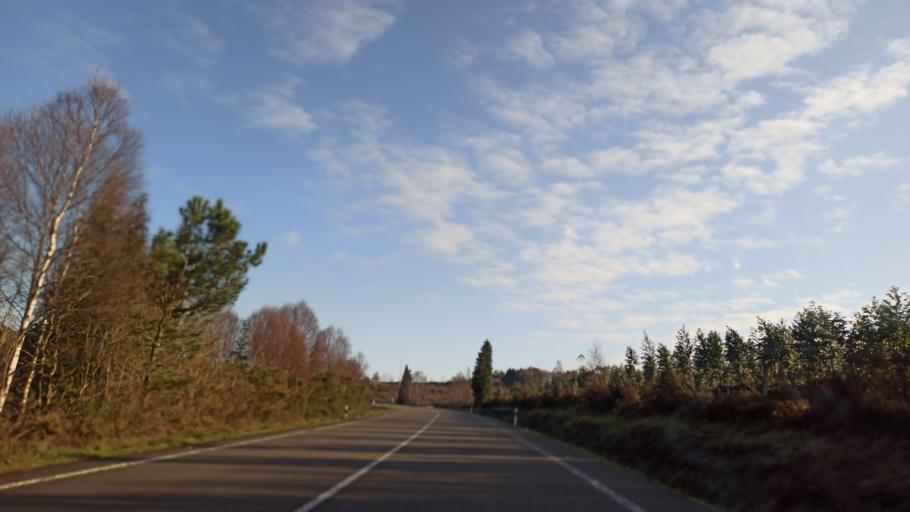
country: ES
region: Galicia
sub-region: Provincia da Coruna
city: As Pontes de Garcia Rodriguez
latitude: 43.4845
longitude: -7.8407
